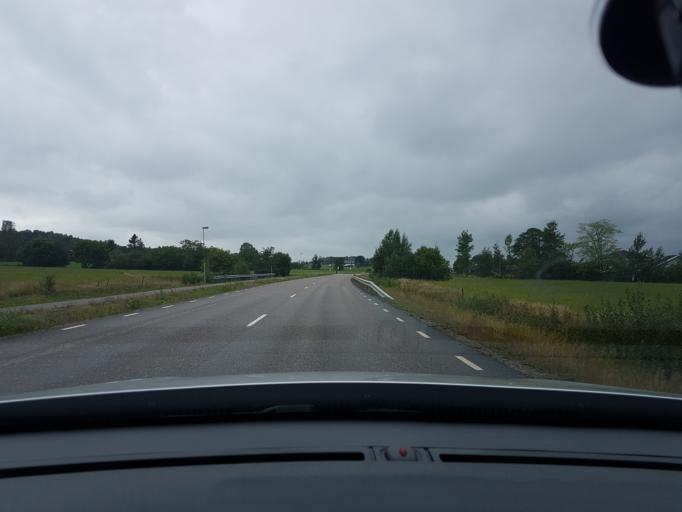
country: SE
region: Vaestra Goetaland
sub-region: Ale Kommun
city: Skepplanda
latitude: 57.9737
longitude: 12.1804
